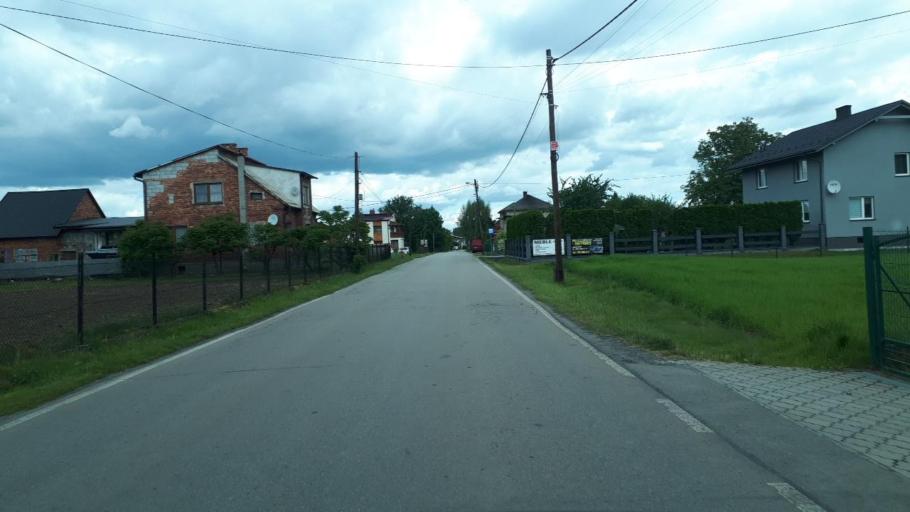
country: PL
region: Silesian Voivodeship
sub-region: Powiat bielski
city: Wilamowice
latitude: 49.9439
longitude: 19.1481
